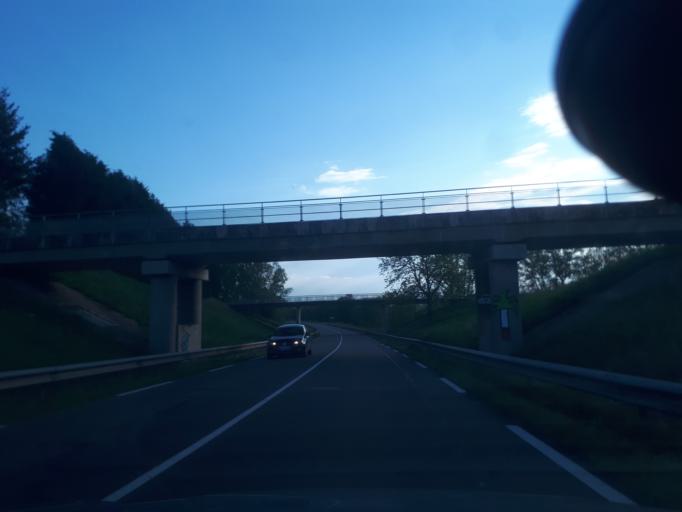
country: FR
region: Bourgogne
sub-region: Departement de Saone-et-Loire
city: Marcigny
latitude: 46.2859
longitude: 4.0342
